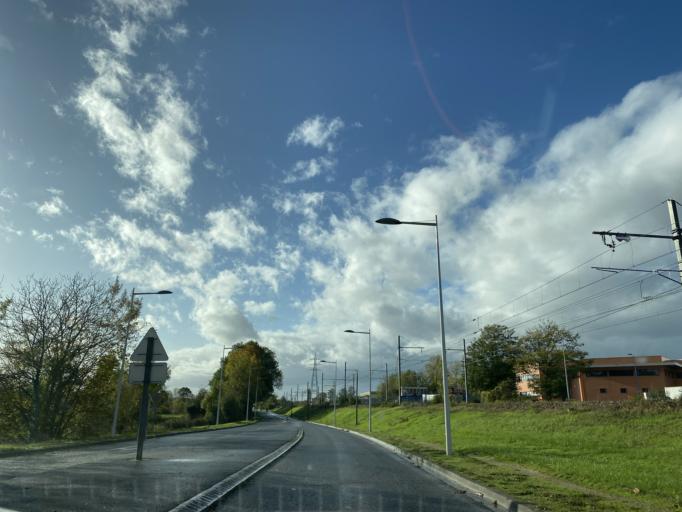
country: FR
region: Centre
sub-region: Departement du Cher
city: Saint-Doulchard
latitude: 47.0947
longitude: 2.3725
